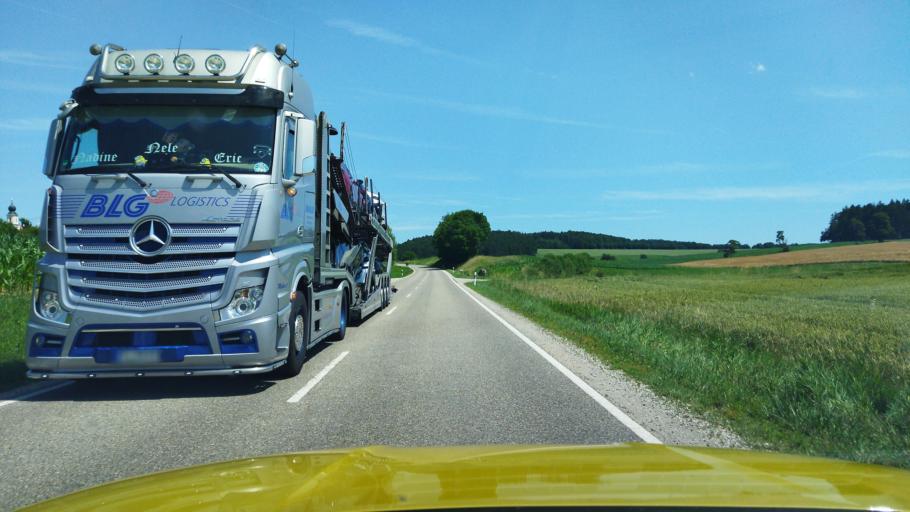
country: DE
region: Bavaria
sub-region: Upper Palatinate
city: Dietfurt
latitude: 48.9474
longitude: 11.5843
